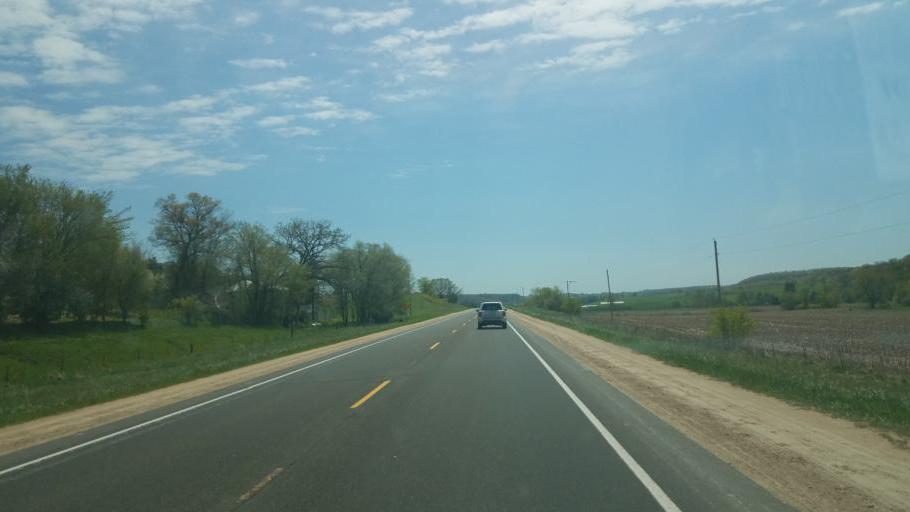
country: US
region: Wisconsin
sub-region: Monroe County
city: Tomah
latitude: 43.8634
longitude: -90.4739
